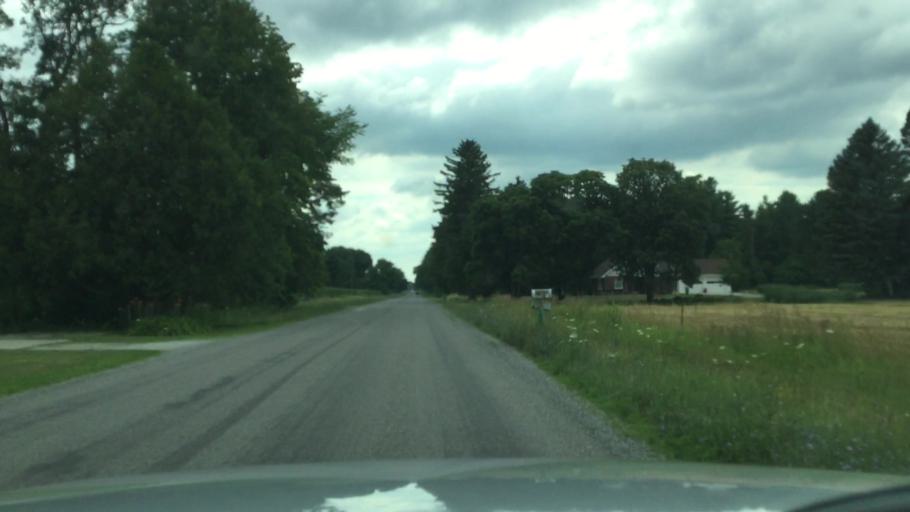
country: US
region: Michigan
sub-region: Saginaw County
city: Frankenmuth
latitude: 43.3217
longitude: -83.7780
